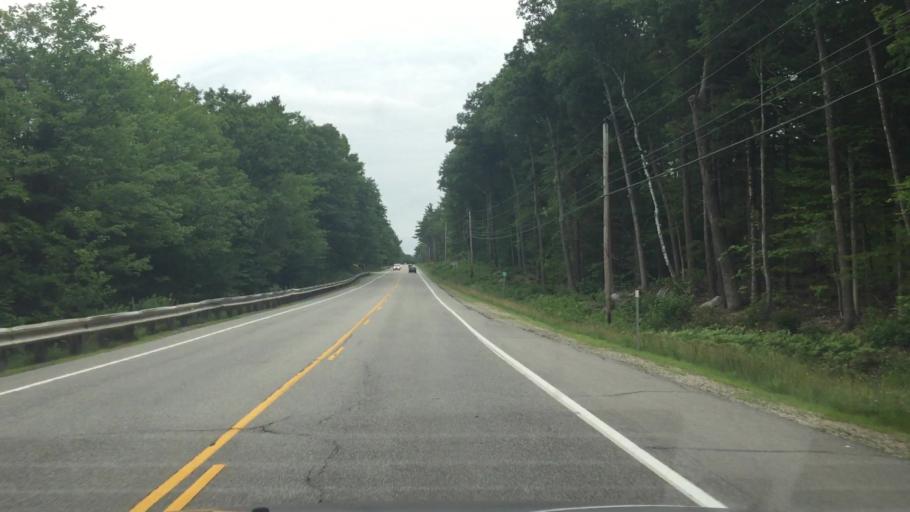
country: US
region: New Hampshire
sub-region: Carroll County
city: Sandwich
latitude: 43.7870
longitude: -71.3778
